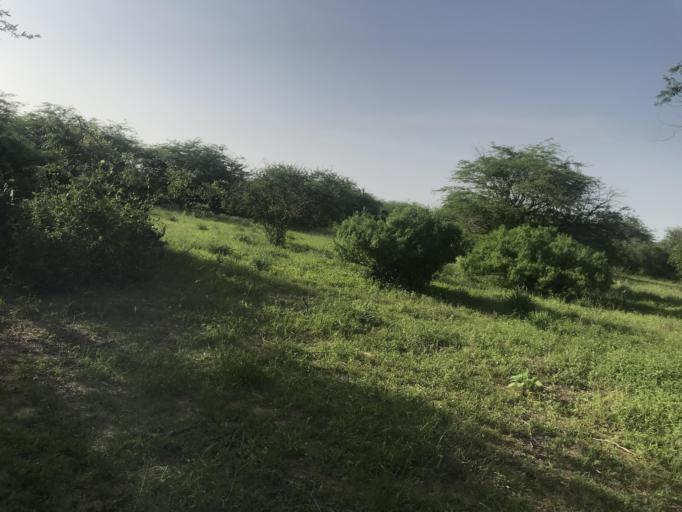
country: SN
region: Saint-Louis
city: Saint-Louis
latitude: 15.9295
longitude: -16.4684
